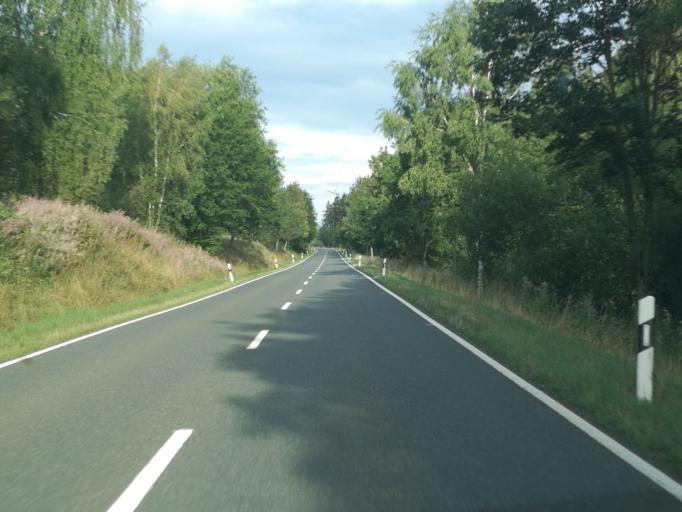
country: DE
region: Bavaria
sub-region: Upper Franconia
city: Regnitzlosau
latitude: 50.3114
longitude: 12.0433
